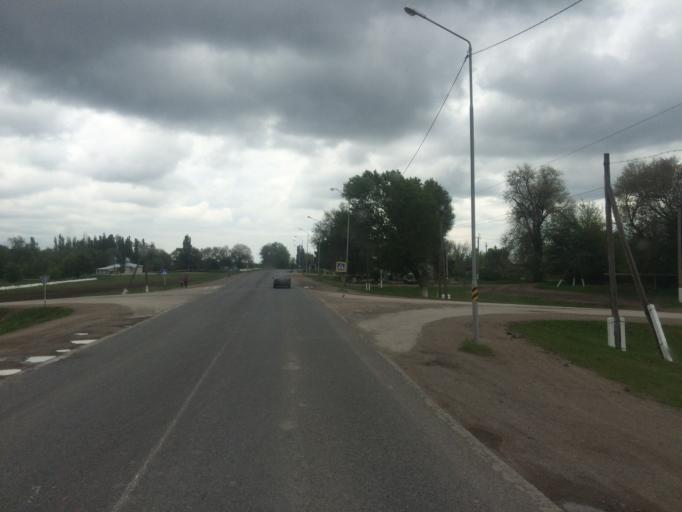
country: KZ
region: Zhambyl
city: Georgiyevka
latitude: 43.1423
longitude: 74.6172
